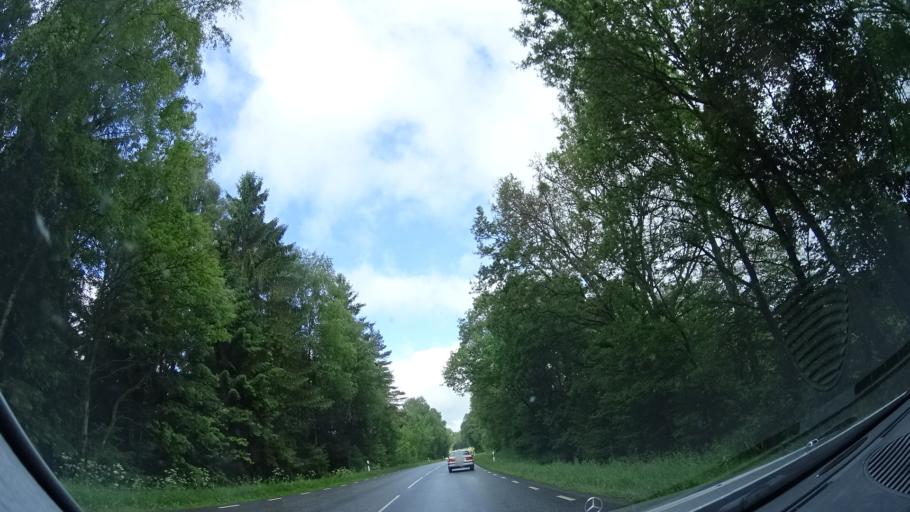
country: SE
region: Skane
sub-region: Eslovs Kommun
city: Stehag
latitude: 55.9431
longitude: 13.4137
